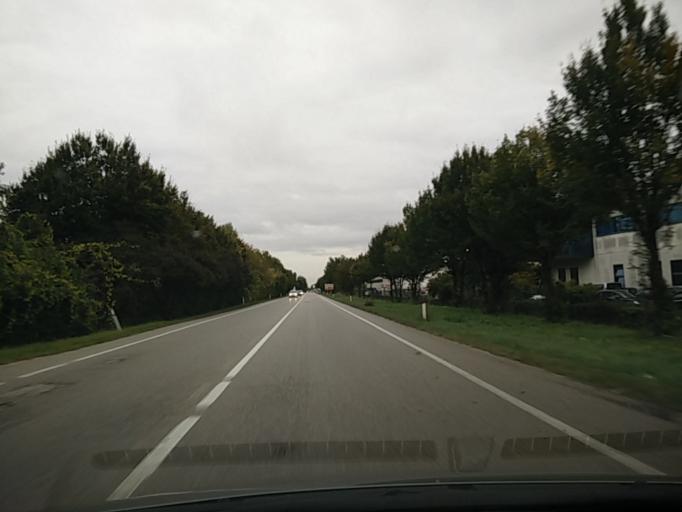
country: IT
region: Veneto
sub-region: Provincia di Treviso
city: Roncade
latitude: 45.6393
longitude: 12.3866
